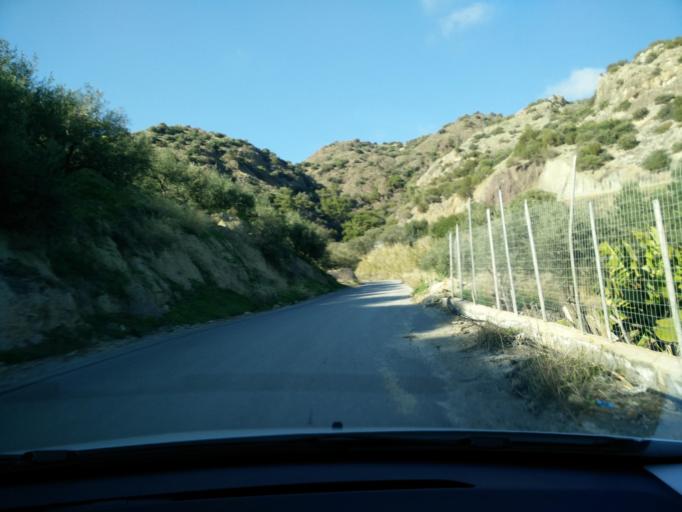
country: GR
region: Crete
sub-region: Nomos Lasithiou
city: Gra Liyia
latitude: 34.9956
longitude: 25.5263
